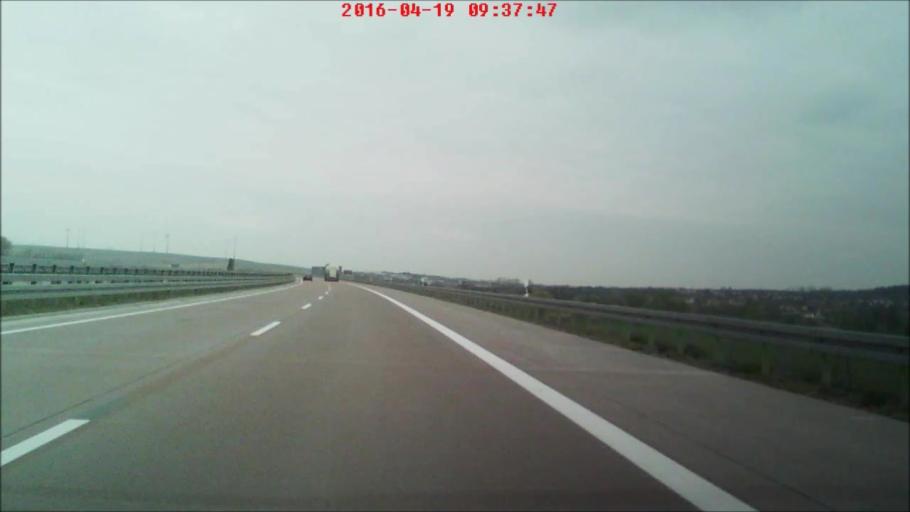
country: DE
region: Thuringia
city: Reinsdorf
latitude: 51.3545
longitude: 11.2701
